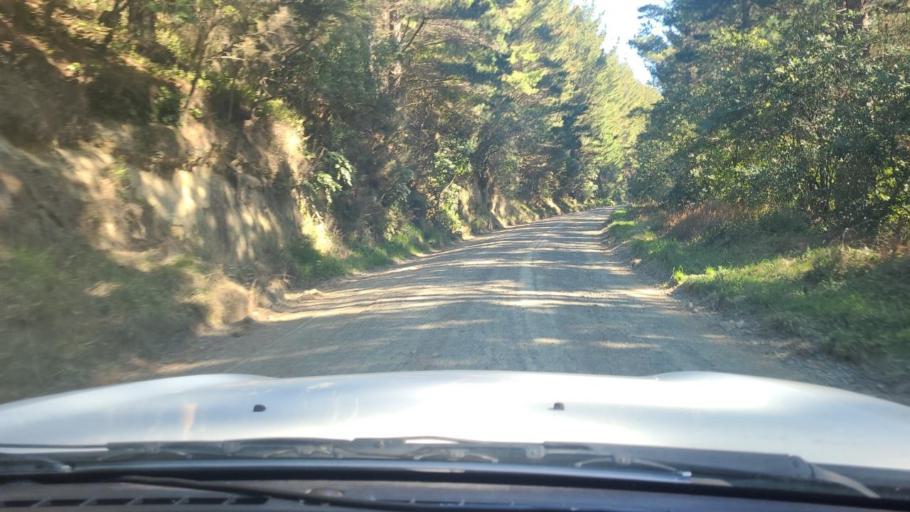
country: NZ
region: Hawke's Bay
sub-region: Napier City
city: Taradale
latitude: -39.4078
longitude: 176.4770
